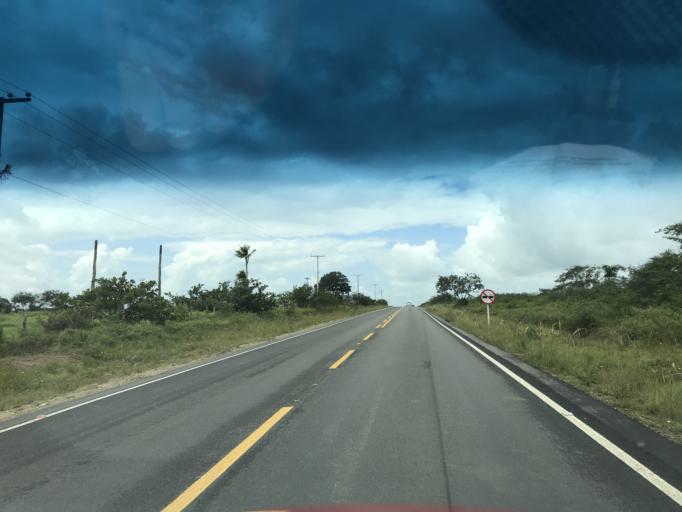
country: BR
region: Bahia
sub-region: Conceicao Do Almeida
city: Conceicao do Almeida
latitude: -12.6715
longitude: -39.2727
